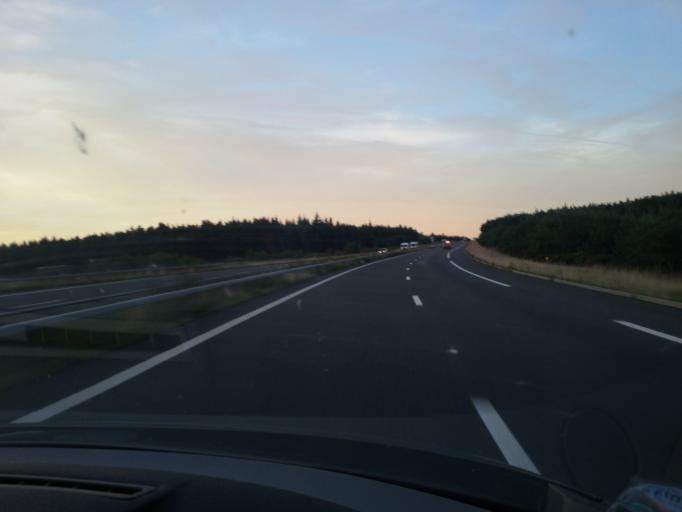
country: FR
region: Languedoc-Roussillon
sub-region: Departement de la Lozere
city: Aumont-Aubrac
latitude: 44.7660
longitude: 3.2831
